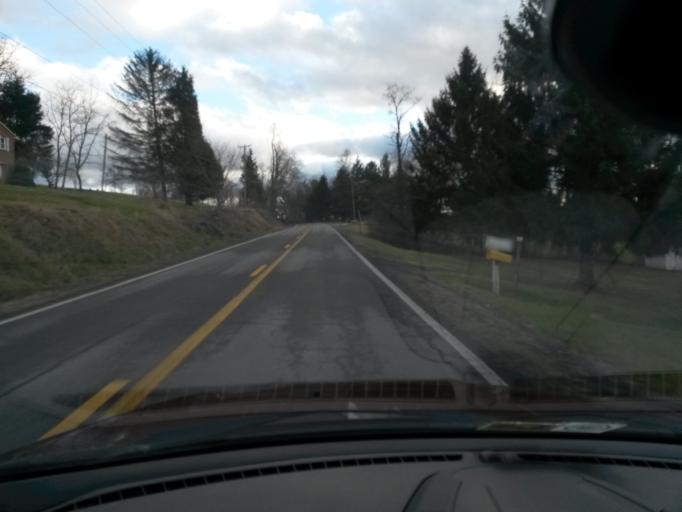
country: US
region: West Virginia
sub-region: Monroe County
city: Union
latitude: 37.5842
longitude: -80.5052
